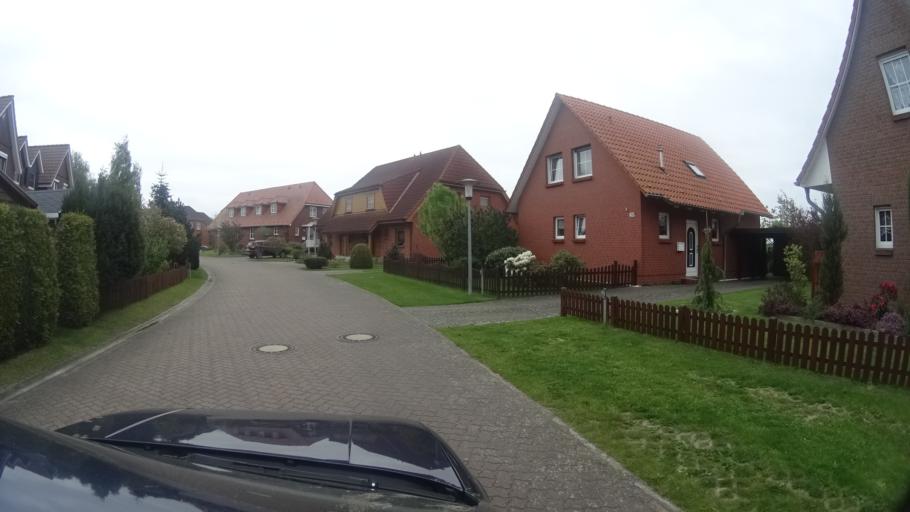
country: DE
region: Mecklenburg-Vorpommern
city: Ribnitz-Damgarten
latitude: 54.2357
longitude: 12.4177
